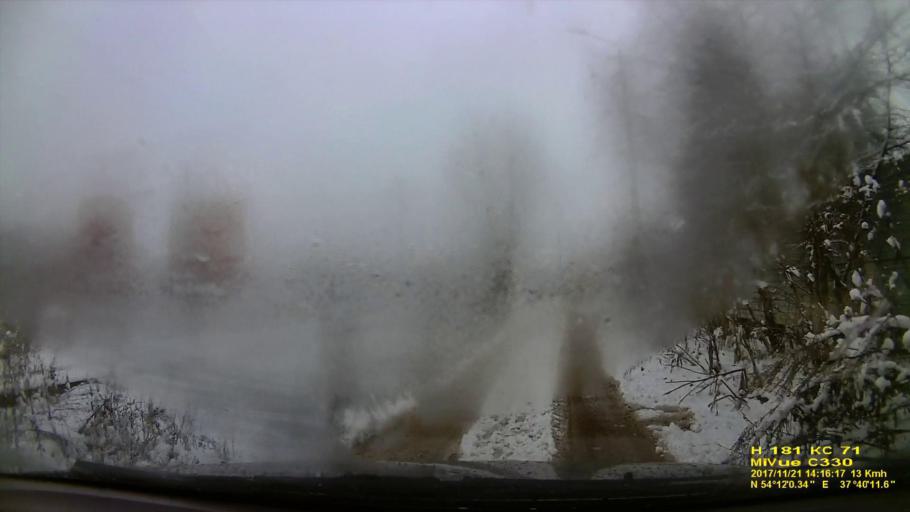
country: RU
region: Tula
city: Tula
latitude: 54.2001
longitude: 37.6699
